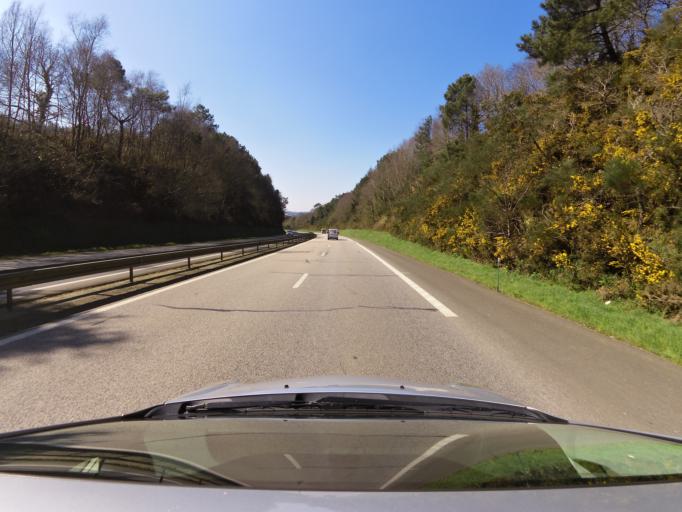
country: FR
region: Brittany
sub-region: Departement du Morbihan
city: Baud
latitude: 47.8844
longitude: -3.0420
